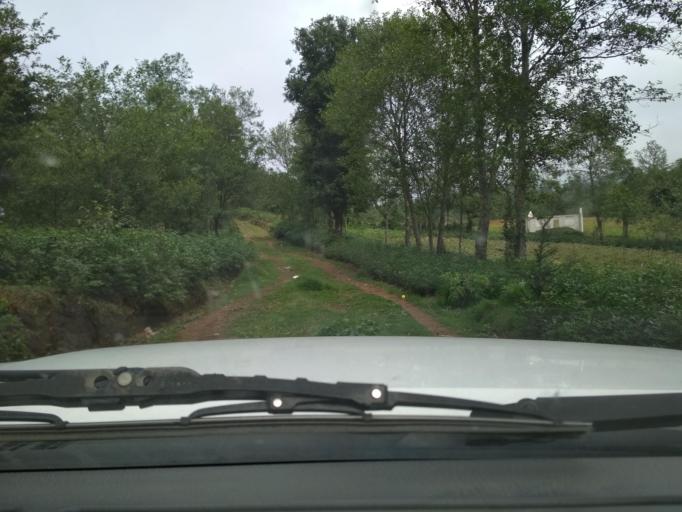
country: MX
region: Veracruz
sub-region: La Perla
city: Chilapa
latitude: 18.9892
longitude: -97.1640
